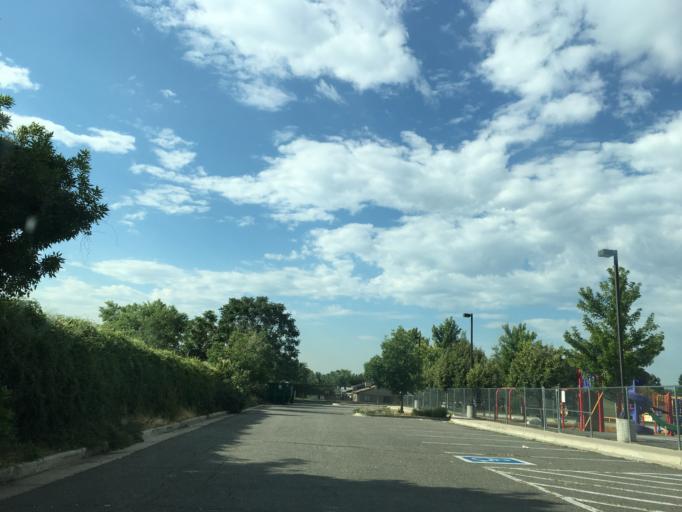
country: US
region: Colorado
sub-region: Arapahoe County
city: Sheridan
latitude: 39.6923
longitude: -105.0333
